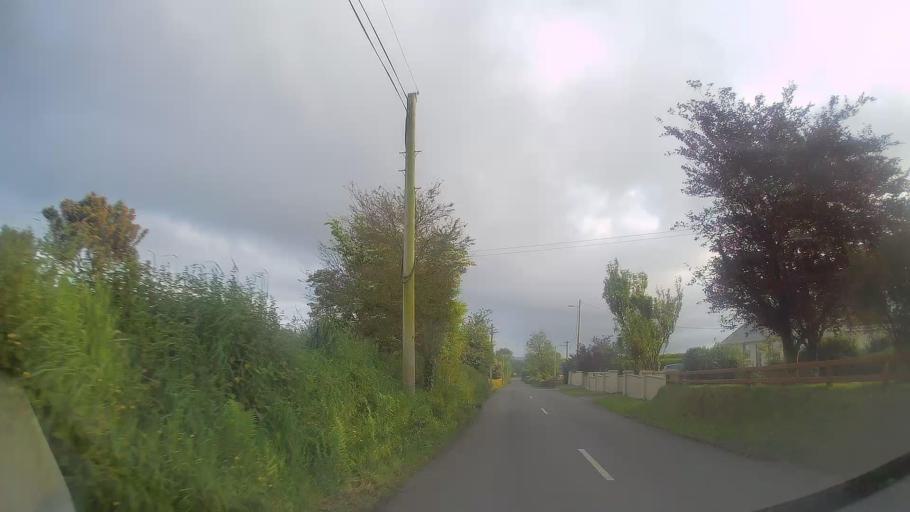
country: IE
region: Munster
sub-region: County Cork
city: Blarney
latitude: 51.9767
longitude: -8.5526
